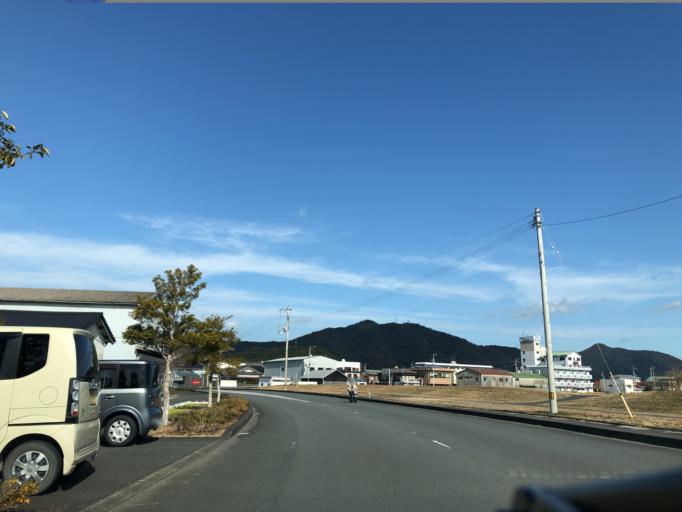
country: JP
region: Kochi
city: Sukumo
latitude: 32.9239
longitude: 132.7027
